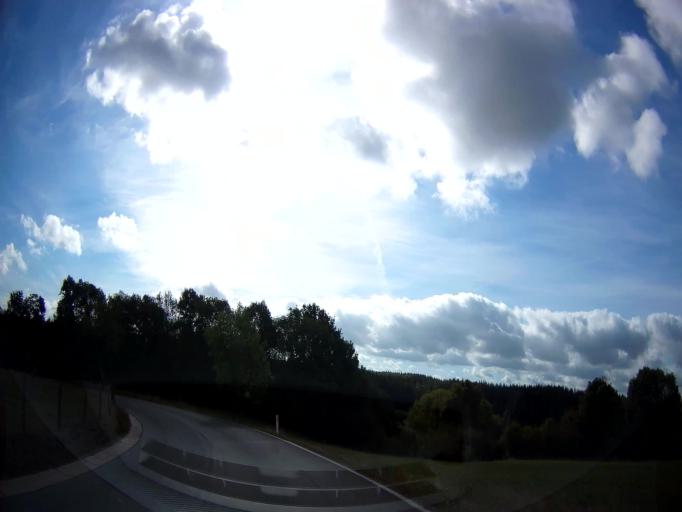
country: BE
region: Wallonia
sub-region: Province du Luxembourg
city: Wellin
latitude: 50.1703
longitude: 5.1262
